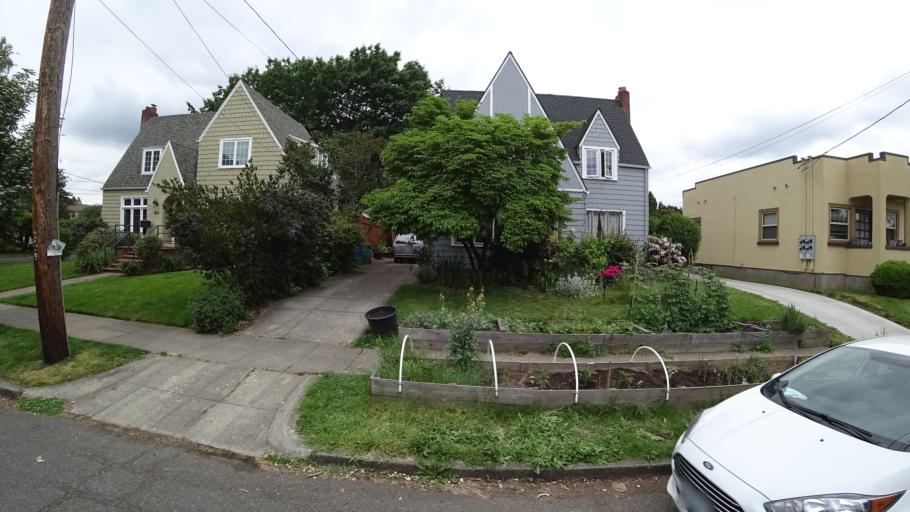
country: US
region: Oregon
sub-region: Multnomah County
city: Portland
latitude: 45.5170
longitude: -122.6217
